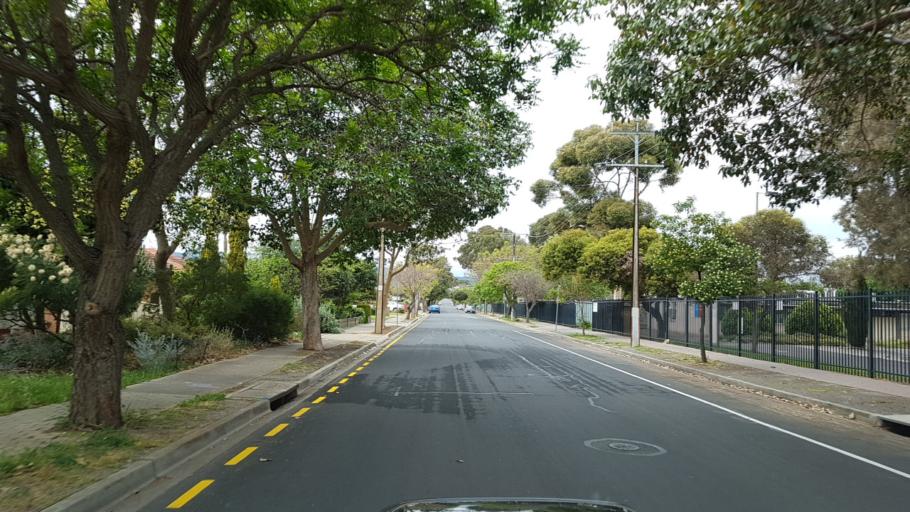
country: AU
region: South Australia
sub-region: Norwood Payneham St Peters
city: Marden
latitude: -34.8904
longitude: 138.6365
